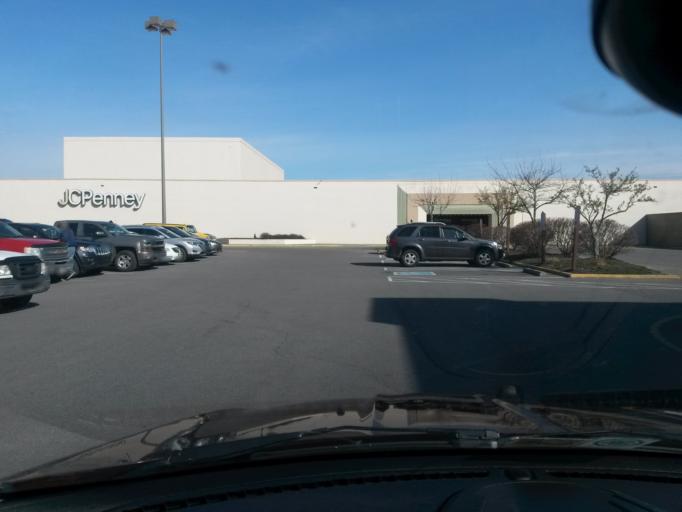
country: US
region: West Virginia
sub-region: Raleigh County
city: Prosperity
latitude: 37.8453
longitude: -81.1982
